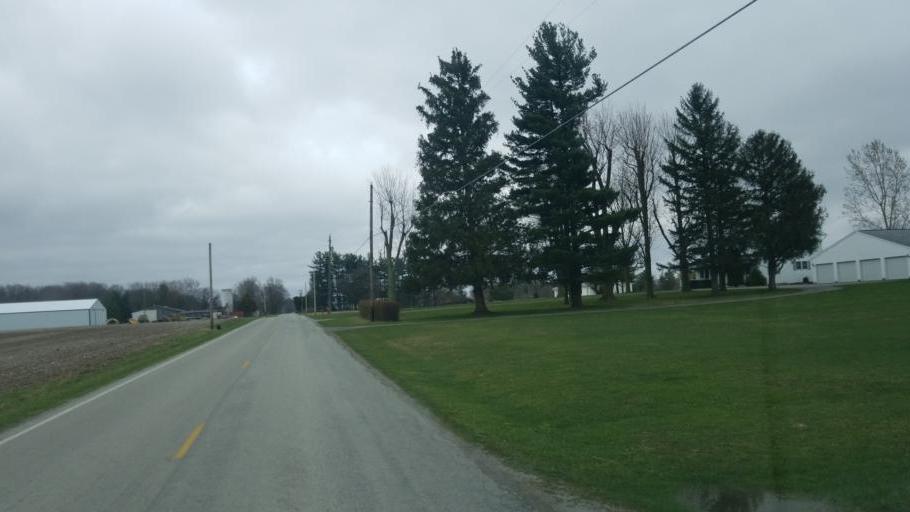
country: US
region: Ohio
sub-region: Wyandot County
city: Upper Sandusky
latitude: 40.8262
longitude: -83.1411
